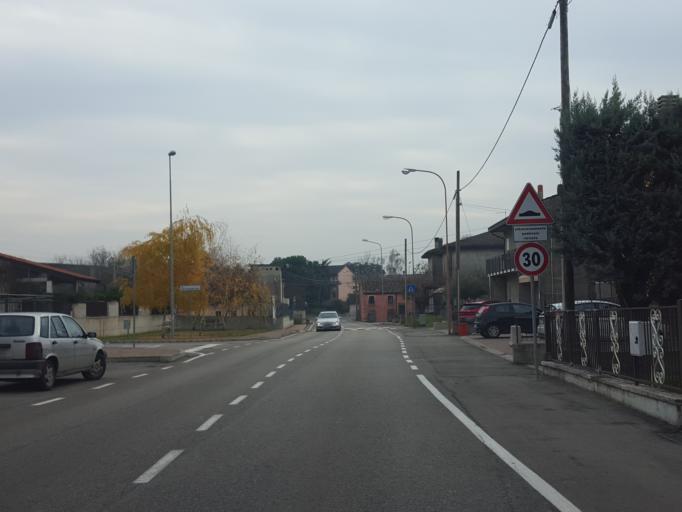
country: IT
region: Veneto
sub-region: Provincia di Verona
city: Arcole
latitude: 45.3662
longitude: 11.2848
